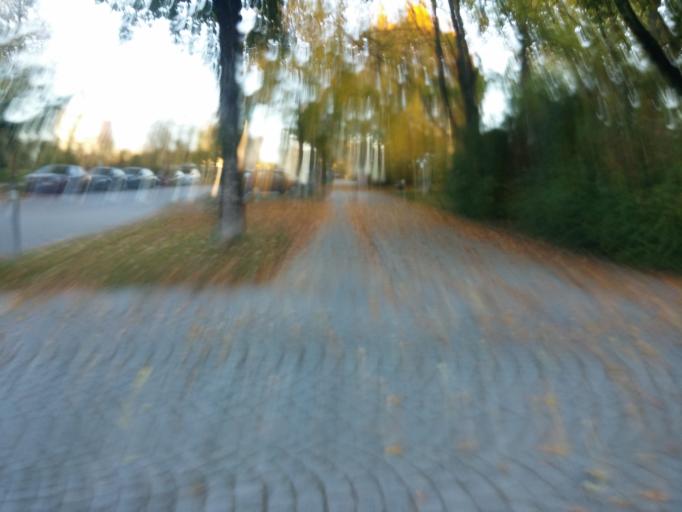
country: DE
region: Bavaria
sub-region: Upper Bavaria
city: Haar
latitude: 48.1042
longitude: 11.7244
